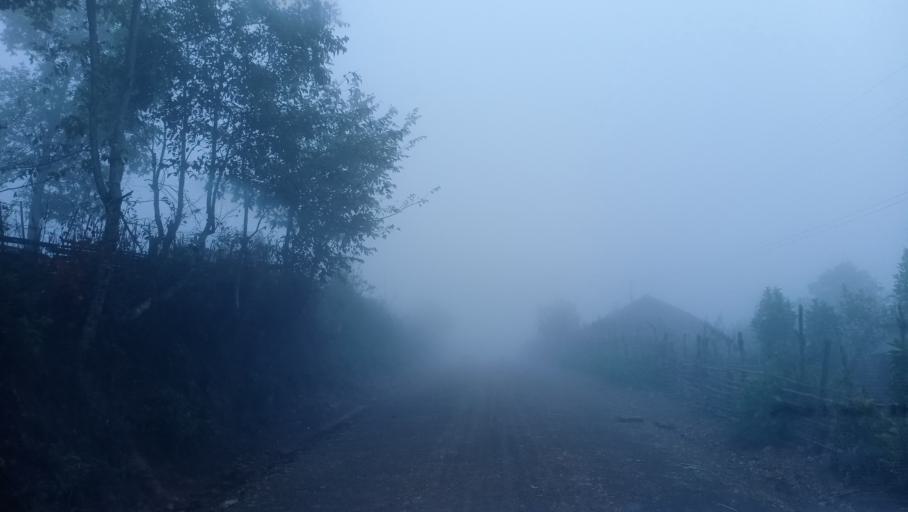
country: LA
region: Phongsali
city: Phongsali
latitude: 21.5028
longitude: 102.1721
